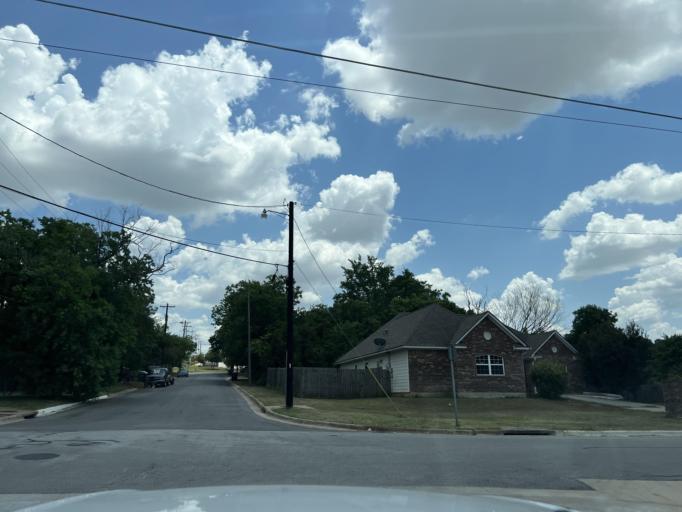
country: US
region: Texas
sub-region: Washington County
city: Brenham
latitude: 30.1735
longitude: -96.3980
